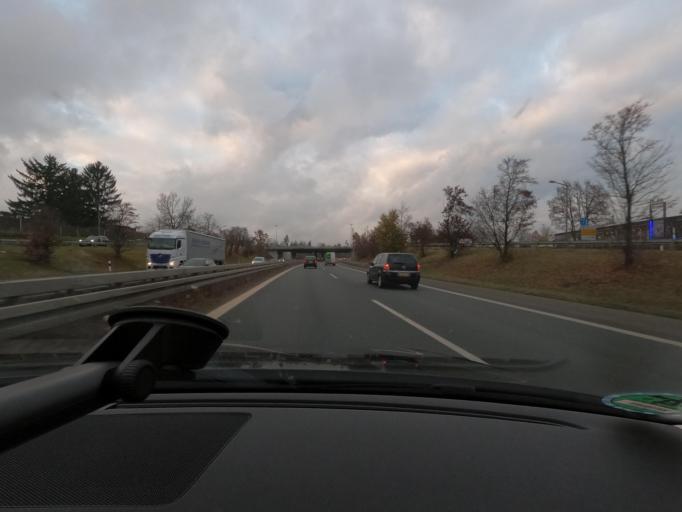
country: DE
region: Bavaria
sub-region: Regierungsbezirk Mittelfranken
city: Furth
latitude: 49.4803
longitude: 11.0064
